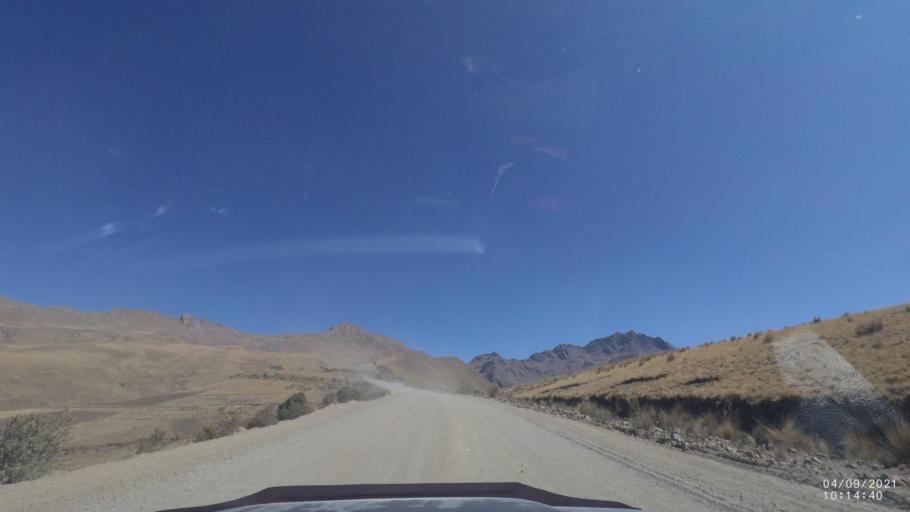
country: BO
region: Cochabamba
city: Sipe Sipe
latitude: -17.3287
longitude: -66.4103
